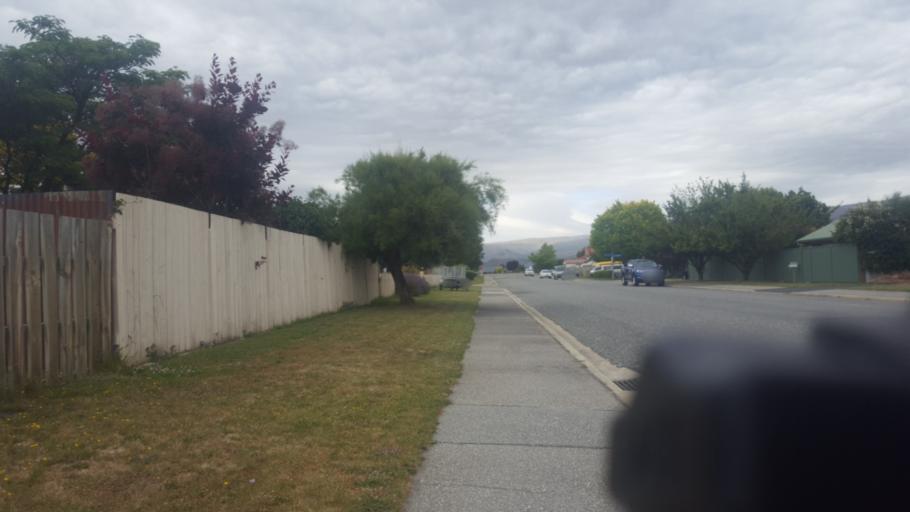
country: NZ
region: Otago
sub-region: Queenstown-Lakes District
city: Wanaka
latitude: -45.0452
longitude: 169.2004
